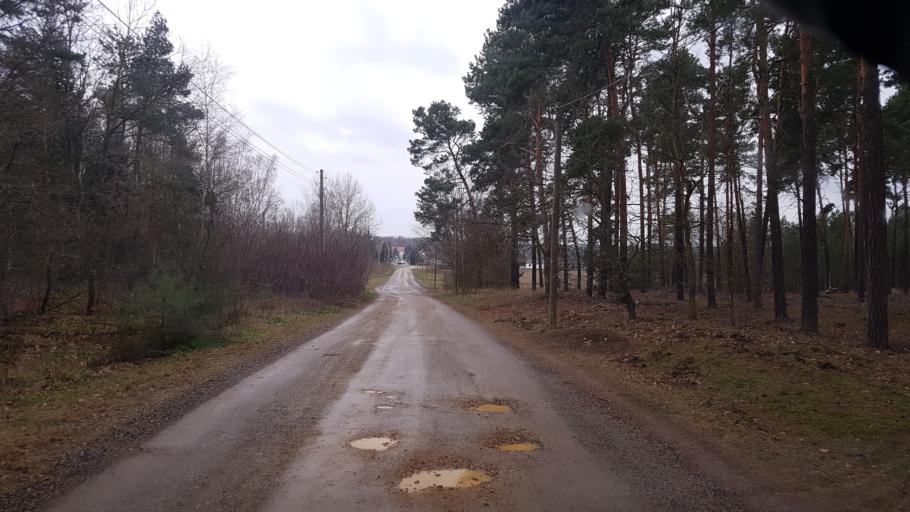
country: DE
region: Brandenburg
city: Crinitz
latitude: 51.7438
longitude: 13.7675
